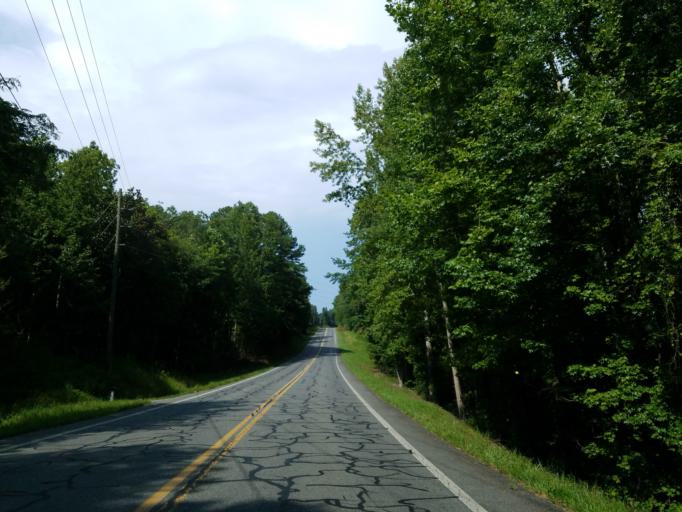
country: US
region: Georgia
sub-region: Gilmer County
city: Ellijay
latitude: 34.5837
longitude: -84.6019
